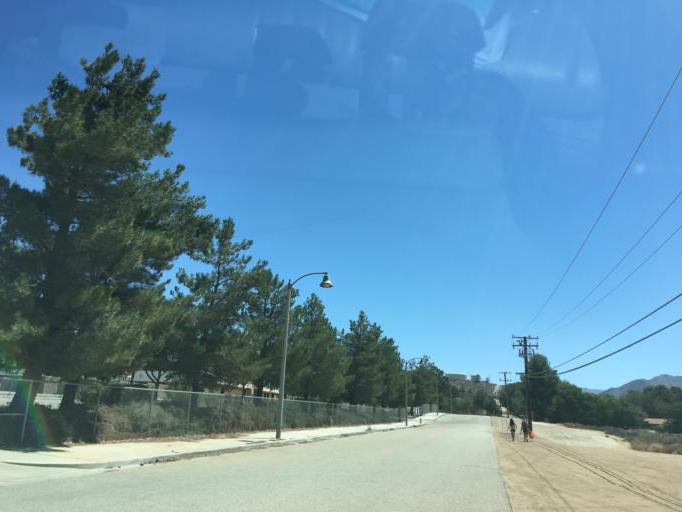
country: US
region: California
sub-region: Los Angeles County
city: Acton
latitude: 34.4736
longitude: -118.1869
